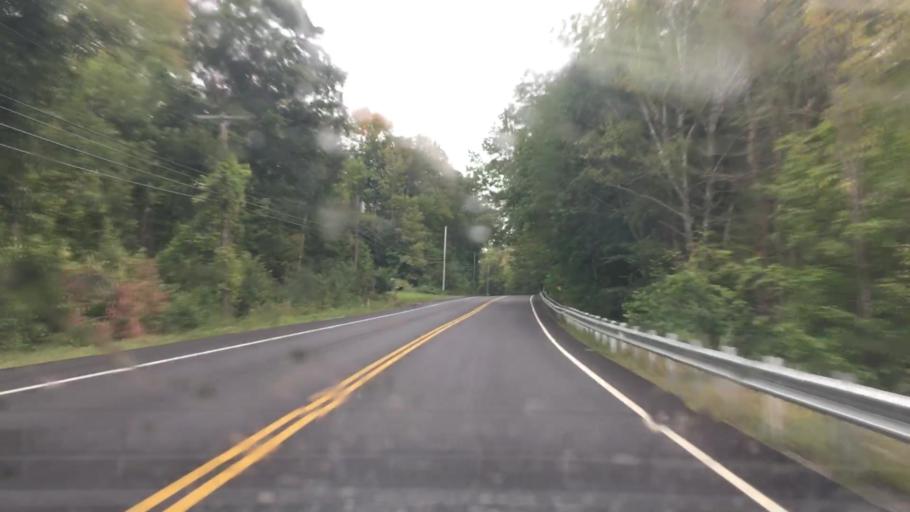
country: US
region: Maine
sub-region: Penobscot County
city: Orrington
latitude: 44.6813
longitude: -68.8086
